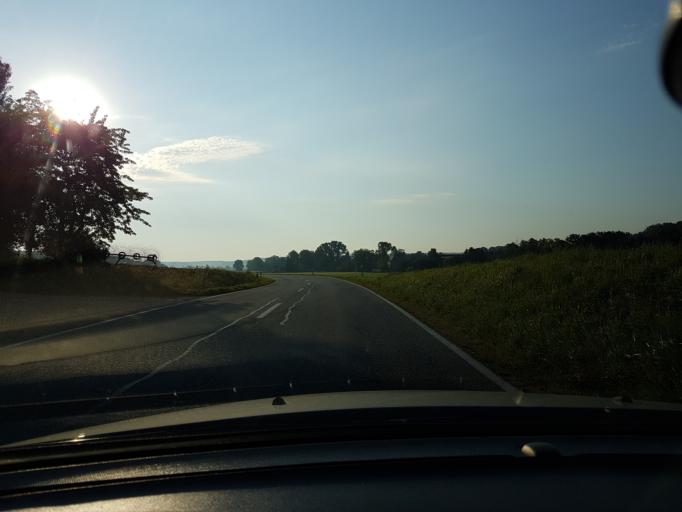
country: DE
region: Bavaria
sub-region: Lower Bavaria
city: Schalkham
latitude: 48.4980
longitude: 12.3833
